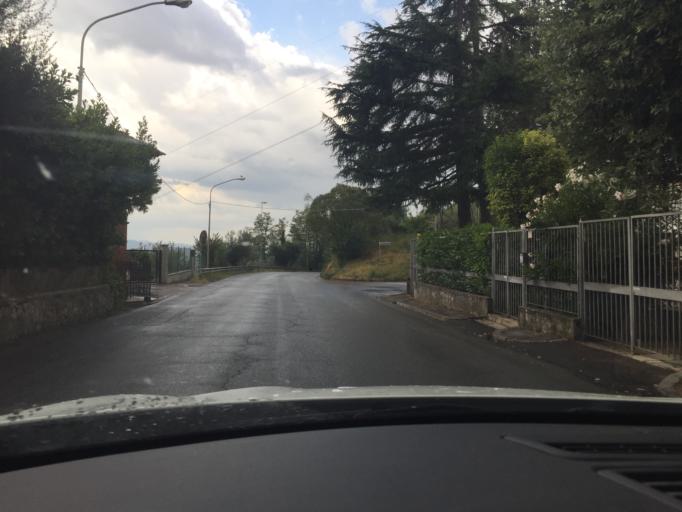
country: IT
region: Umbria
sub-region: Provincia di Perugia
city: Perugia
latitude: 43.0755
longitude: 12.4016
